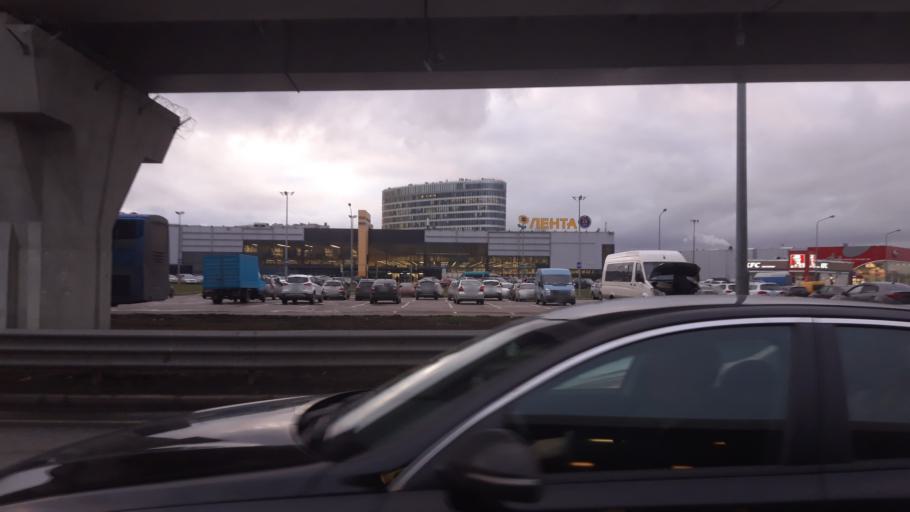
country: RU
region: St.-Petersburg
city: Kupchino
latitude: 59.8086
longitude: 30.3233
